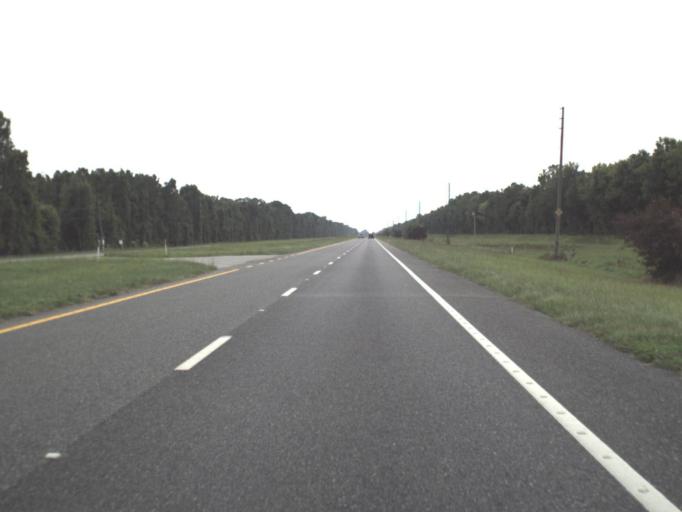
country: US
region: Florida
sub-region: Levy County
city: Inglis
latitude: 29.2161
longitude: -82.7004
